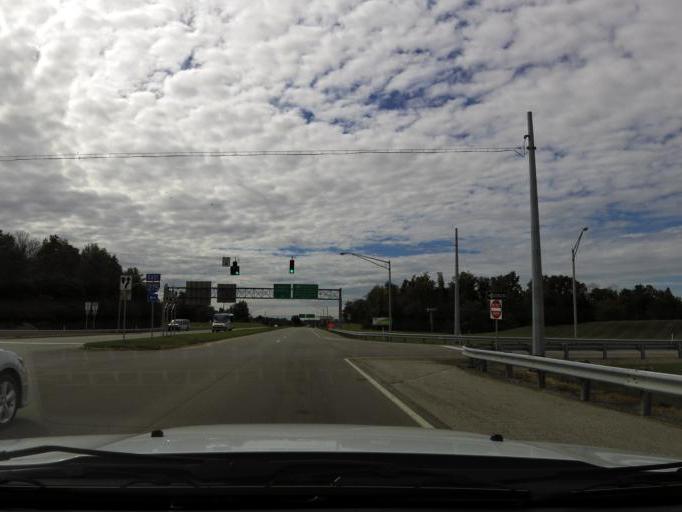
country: US
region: Kentucky
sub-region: Boone County
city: Hebron
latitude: 39.0697
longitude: -84.6550
